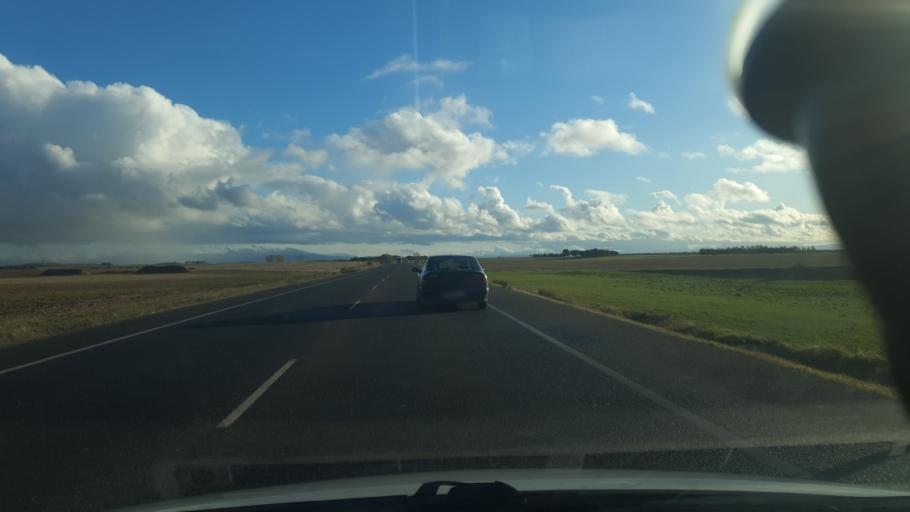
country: ES
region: Castille and Leon
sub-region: Provincia de Segovia
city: Rapariegos
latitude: 41.0849
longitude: -4.6363
